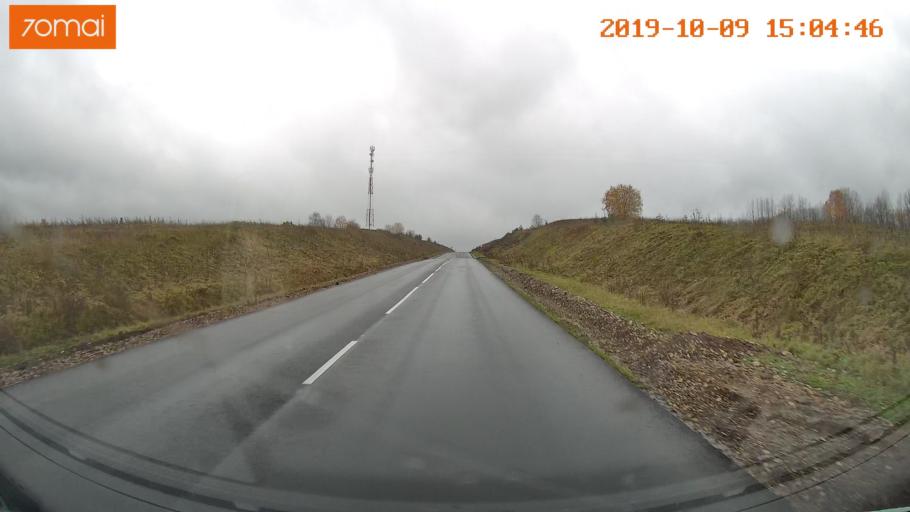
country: RU
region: Kostroma
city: Chistyye Bory
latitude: 58.2544
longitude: 41.6641
